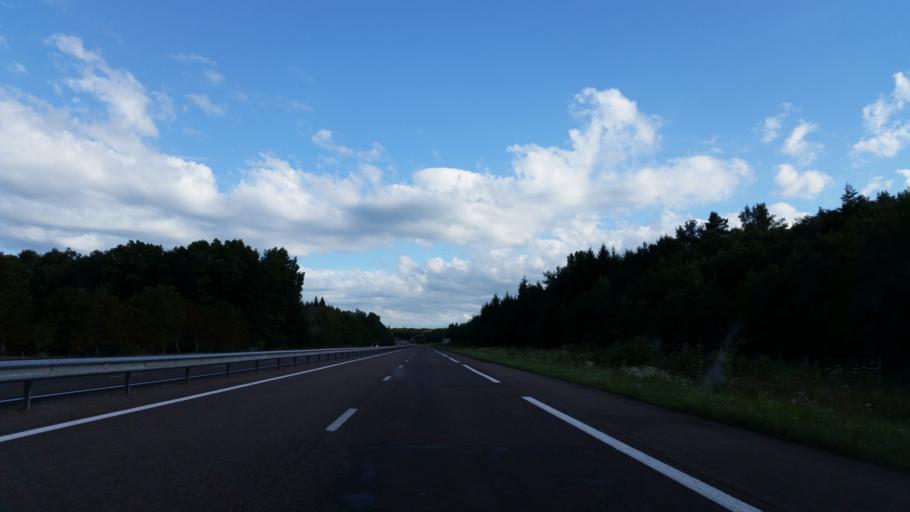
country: FR
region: Franche-Comte
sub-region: Departement de la Haute-Saone
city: Saint-Sauveur
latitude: 47.7437
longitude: 6.4339
